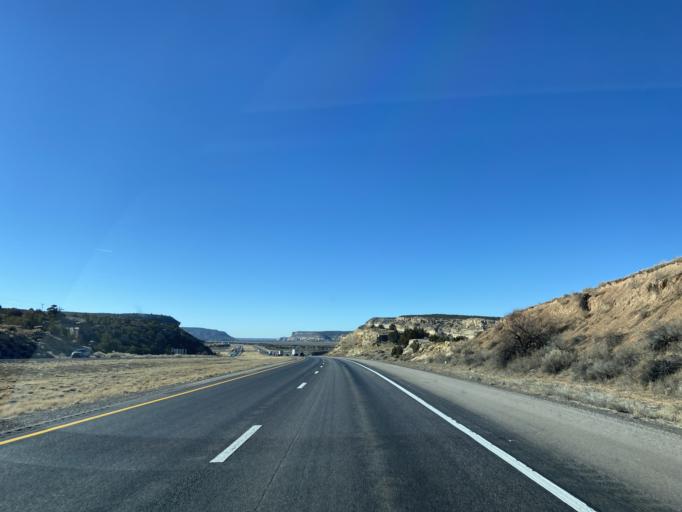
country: US
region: Arizona
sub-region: Apache County
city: Saint Michaels
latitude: 35.4224
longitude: -108.9876
